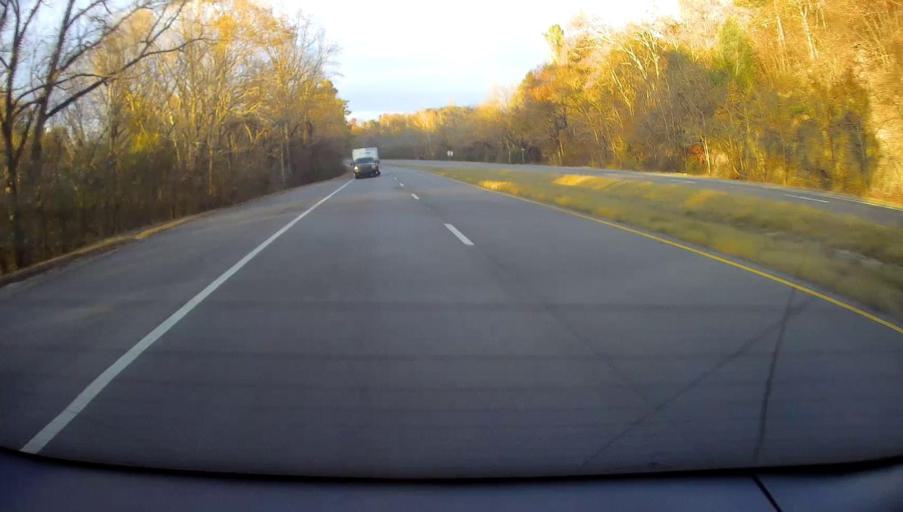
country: US
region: Alabama
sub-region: Etowah County
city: Attalla
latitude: 34.0300
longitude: -86.1108
